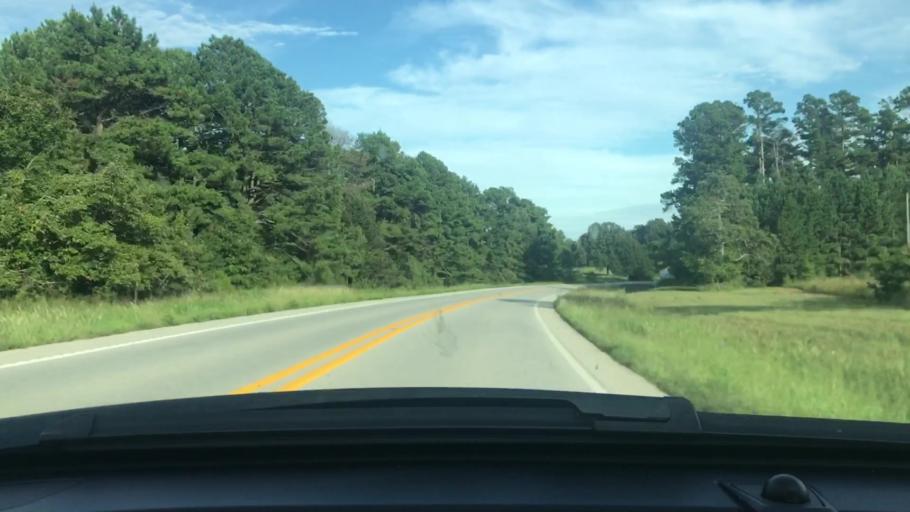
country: US
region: Arkansas
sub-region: Sharp County
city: Cherokee Village
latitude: 36.2765
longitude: -91.3108
